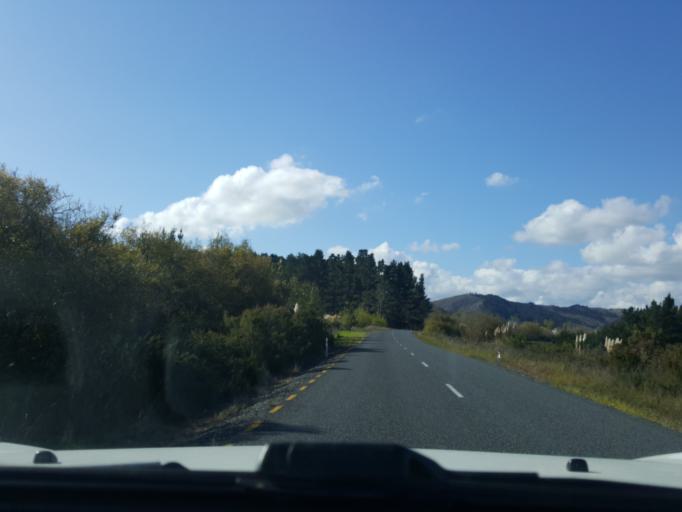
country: NZ
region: Waikato
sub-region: Waikato District
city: Ngaruawahia
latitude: -37.5334
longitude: 175.1791
